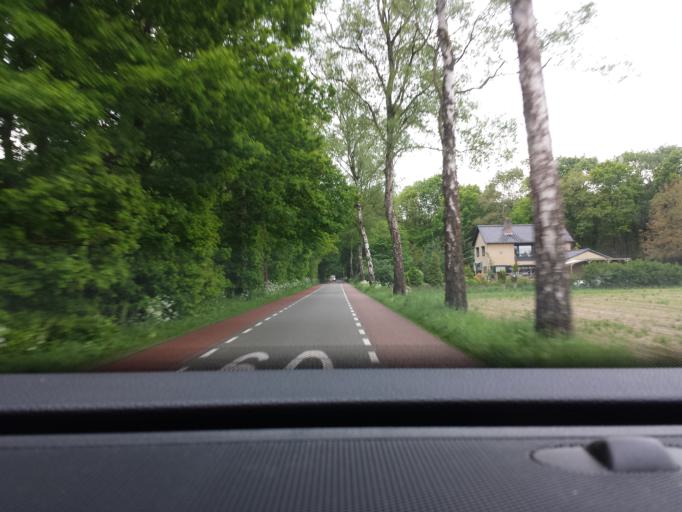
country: NL
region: Gelderland
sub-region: Gemeente Lochem
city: Almen
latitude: 52.1124
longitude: 6.3518
